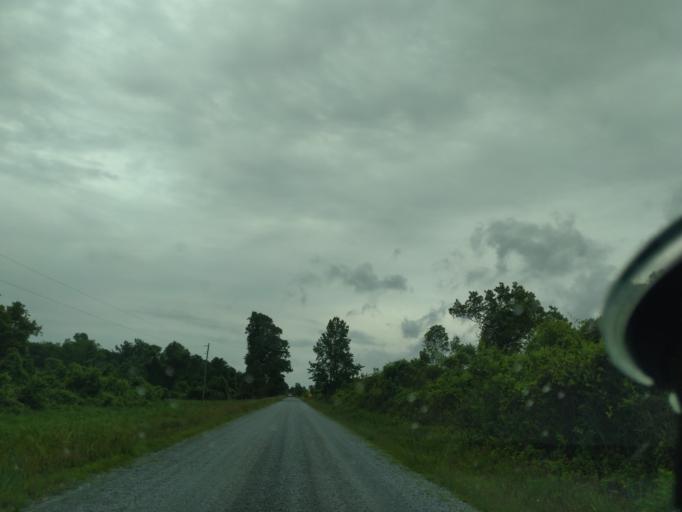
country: US
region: North Carolina
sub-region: Beaufort County
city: Belhaven
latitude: 35.7329
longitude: -76.4469
